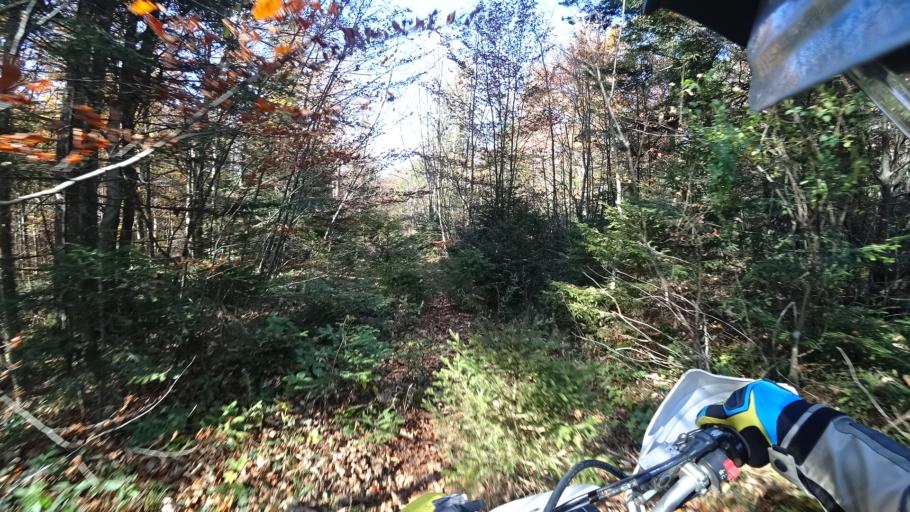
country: HR
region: Karlovacka
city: Plaski
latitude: 45.0701
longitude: 15.3096
